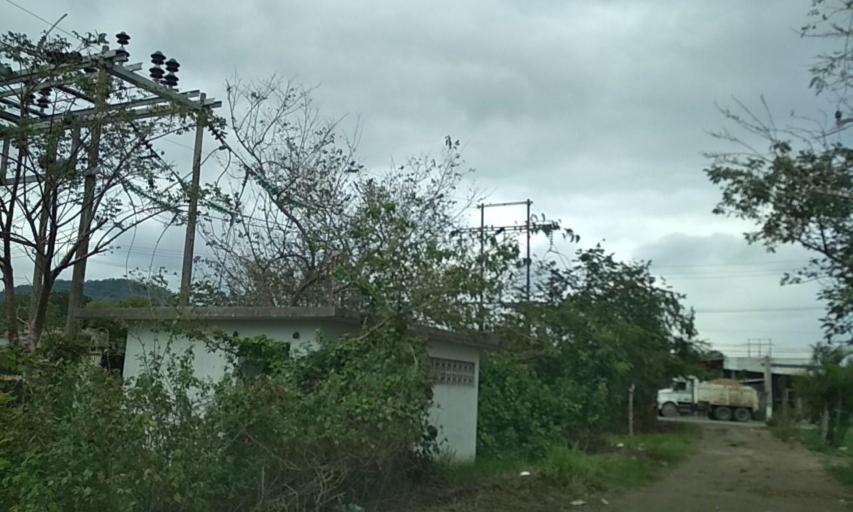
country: MX
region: Veracruz
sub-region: Papantla
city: El Chote
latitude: 20.3970
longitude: -97.3367
